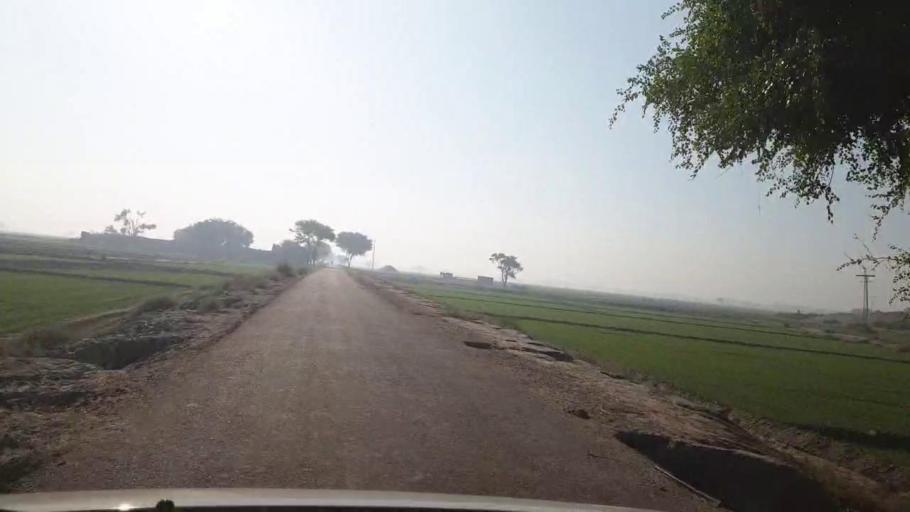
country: PK
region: Sindh
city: Dadu
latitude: 26.6727
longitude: 67.8135
